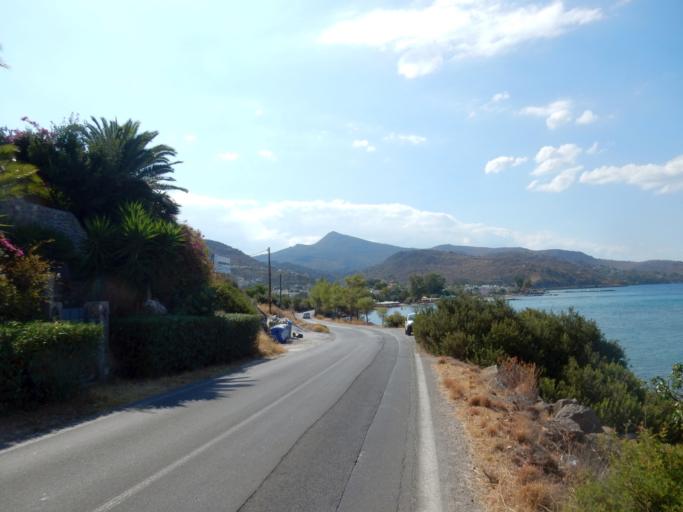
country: GR
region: Attica
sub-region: Nomos Piraios
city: Aegina
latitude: 37.7215
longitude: 23.4564
